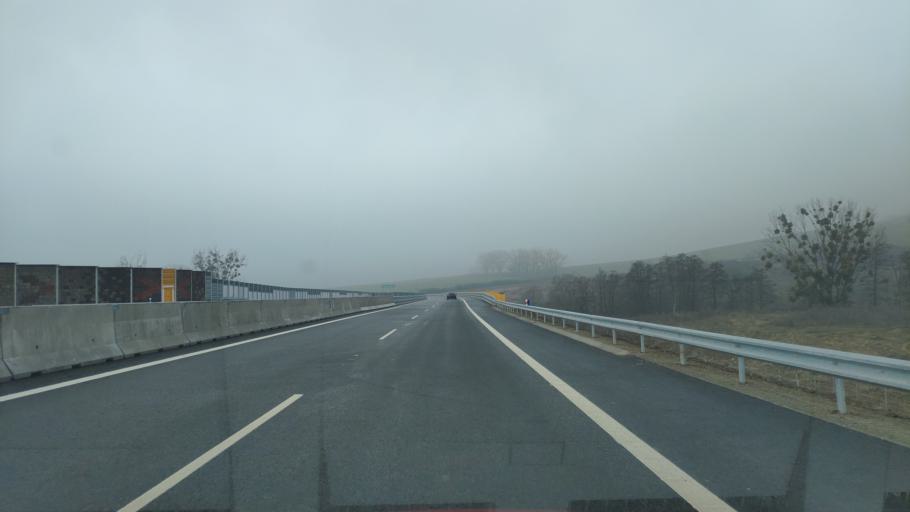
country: SK
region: Kosicky
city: Kosice
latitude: 48.7426
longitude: 21.3669
